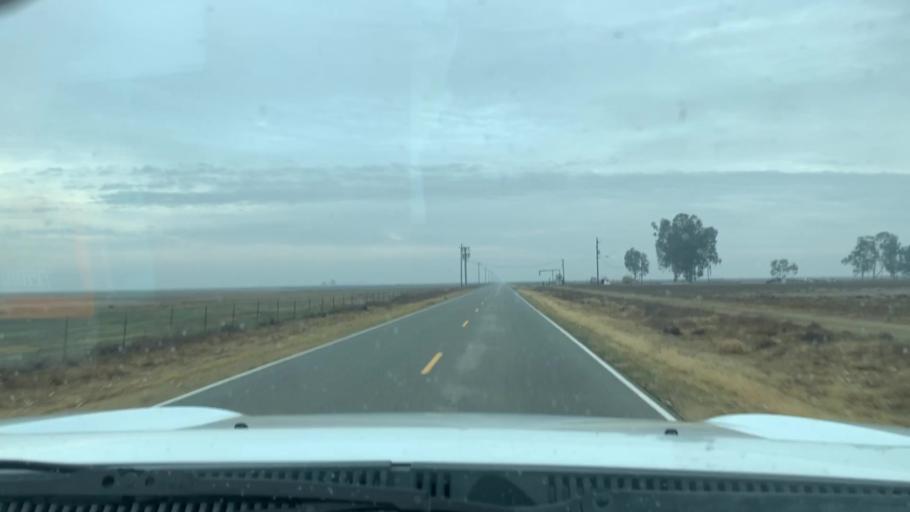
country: US
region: California
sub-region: Kern County
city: Lost Hills
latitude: 35.6649
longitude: -119.5799
